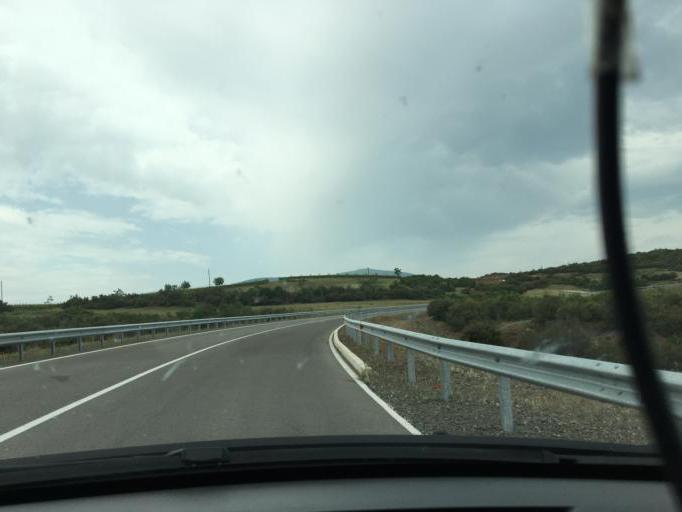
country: MK
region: Gevgelija
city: Miravci
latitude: 41.2999
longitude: 22.4400
